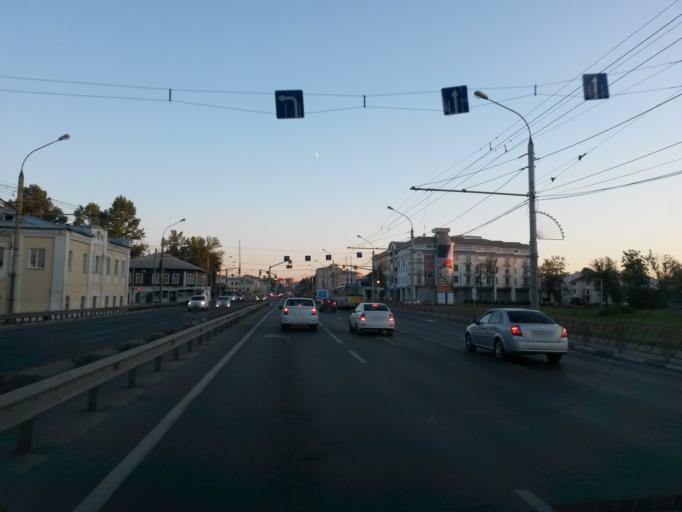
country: RU
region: Jaroslavl
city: Yaroslavl
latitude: 57.6135
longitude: 39.8832
